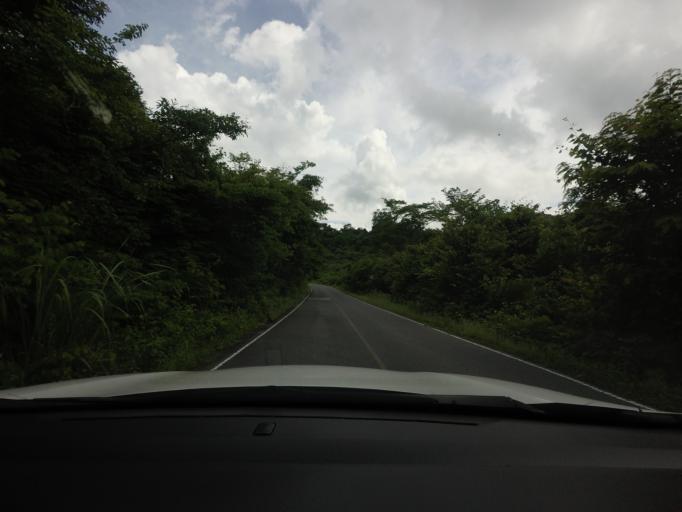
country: TH
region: Nakhon Nayok
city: Pak Phli
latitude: 14.2490
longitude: 101.3857
